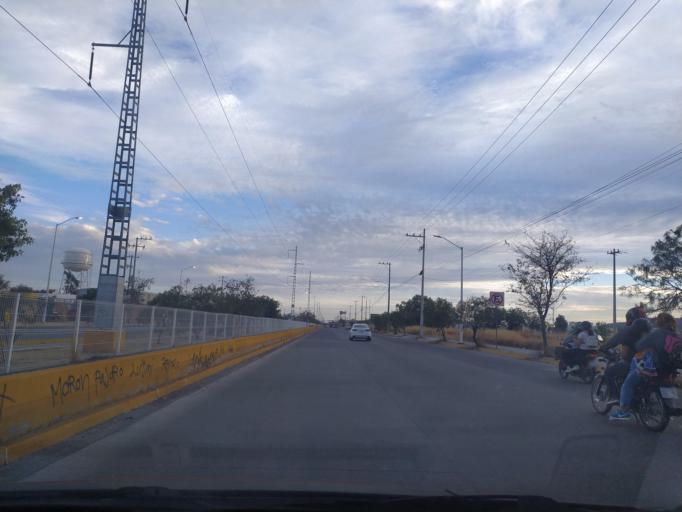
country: LA
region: Oudomxai
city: Muang La
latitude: 21.0210
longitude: 101.8697
